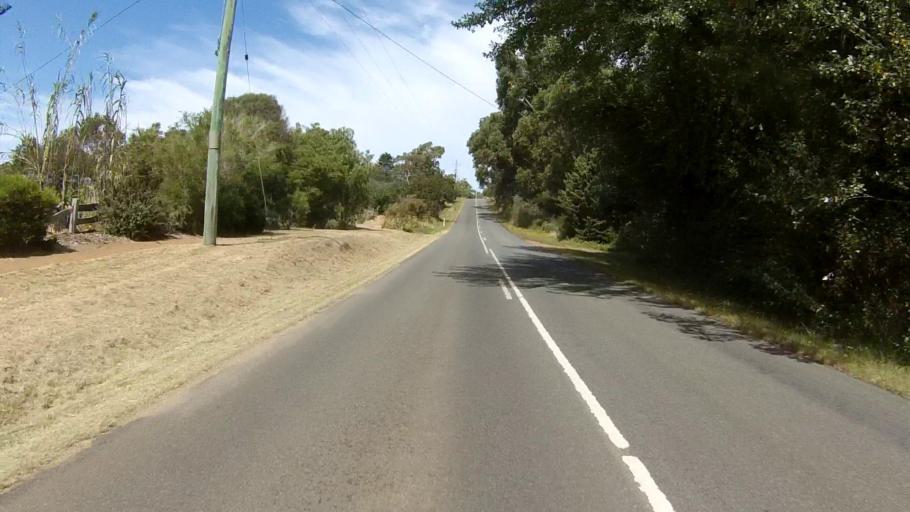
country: AU
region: Tasmania
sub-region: Kingborough
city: Taroona
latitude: -43.0136
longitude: 147.4145
